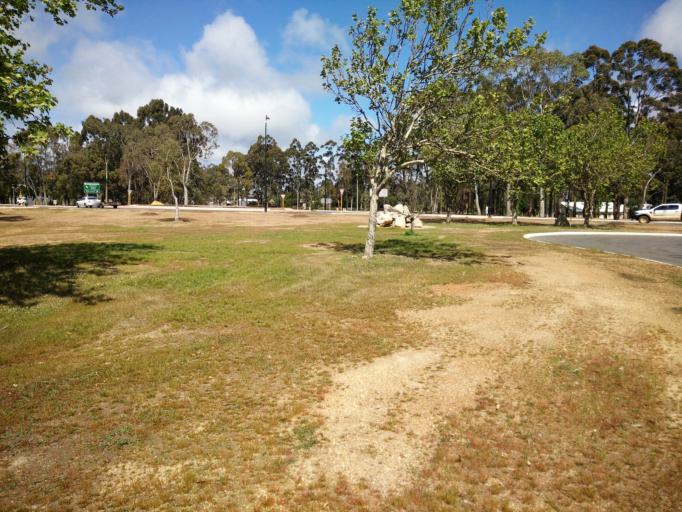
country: AU
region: Western Australia
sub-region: Manjimup
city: Manjimup
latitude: -34.2355
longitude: 116.1499
